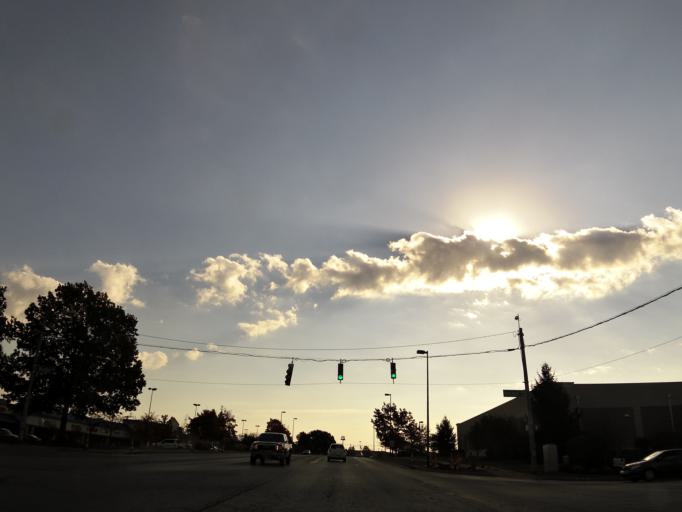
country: US
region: Kentucky
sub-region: Fayette County
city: Lexington-Fayette
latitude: 38.0218
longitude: -84.4213
